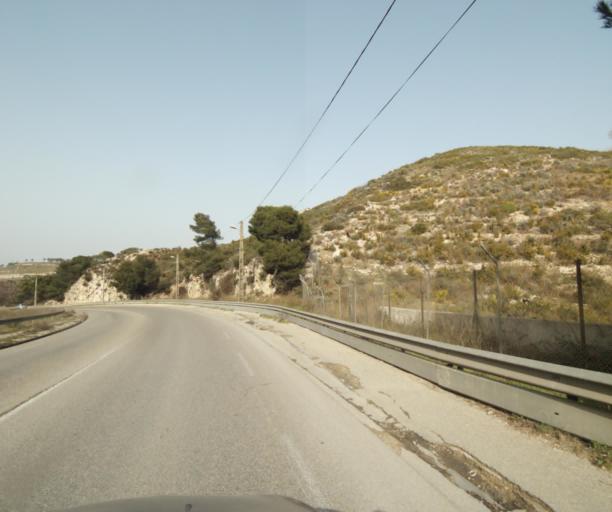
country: FR
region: Provence-Alpes-Cote d'Azur
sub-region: Departement des Bouches-du-Rhone
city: Les Pennes-Mirabeau
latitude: 43.4044
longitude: 5.3324
